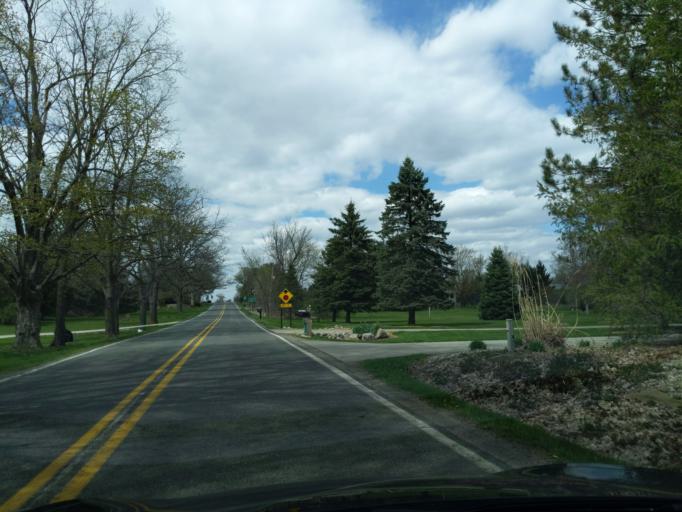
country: US
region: Michigan
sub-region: Ingham County
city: Holt
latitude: 42.6384
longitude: -84.4626
